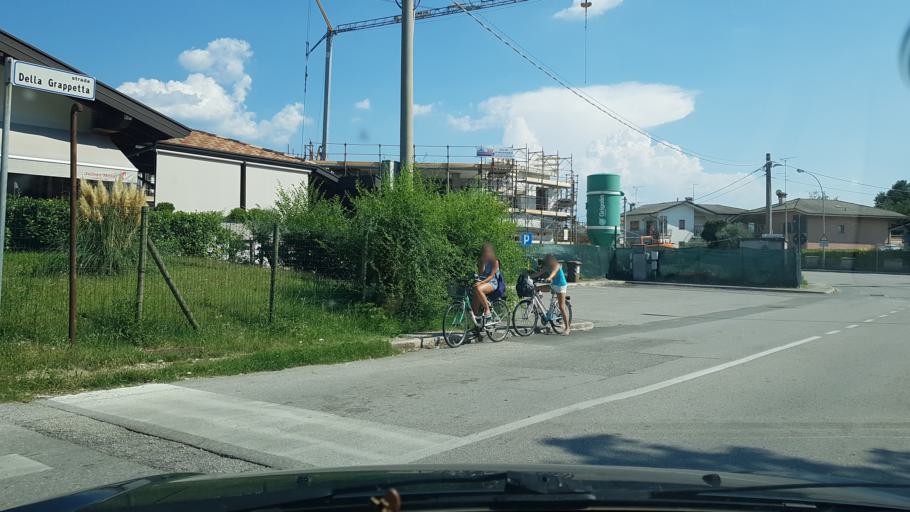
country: IT
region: Friuli Venezia Giulia
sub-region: Provincia di Gorizia
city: Staranzano
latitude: 45.7944
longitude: 13.5034
